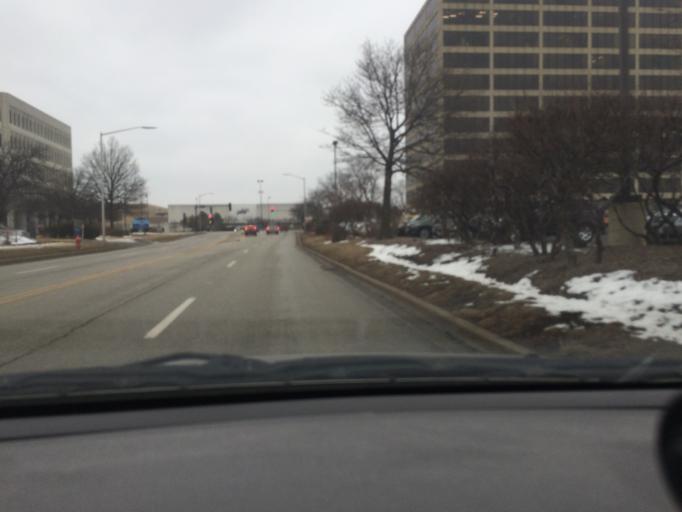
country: US
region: Illinois
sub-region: Cook County
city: Hoffman Estates
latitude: 42.0417
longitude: -88.0389
